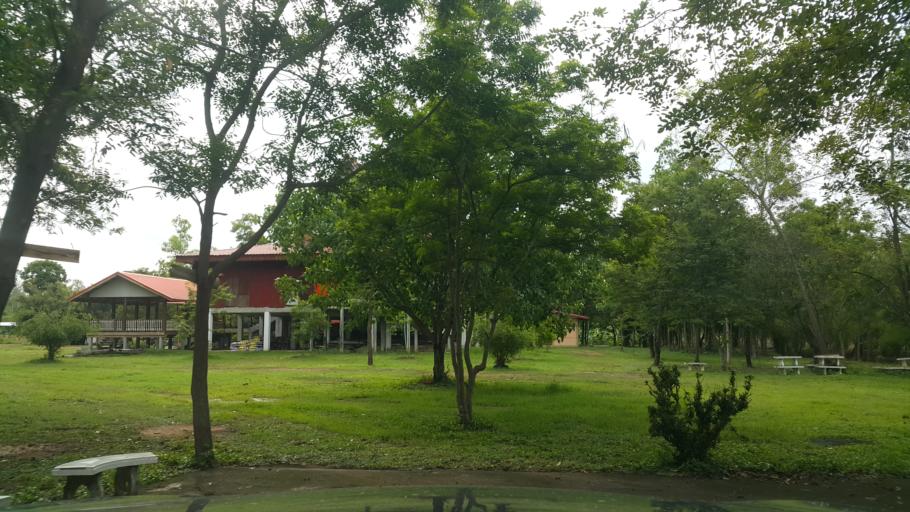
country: TH
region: Sukhothai
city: Sawankhalok
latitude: 17.3119
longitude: 99.7007
